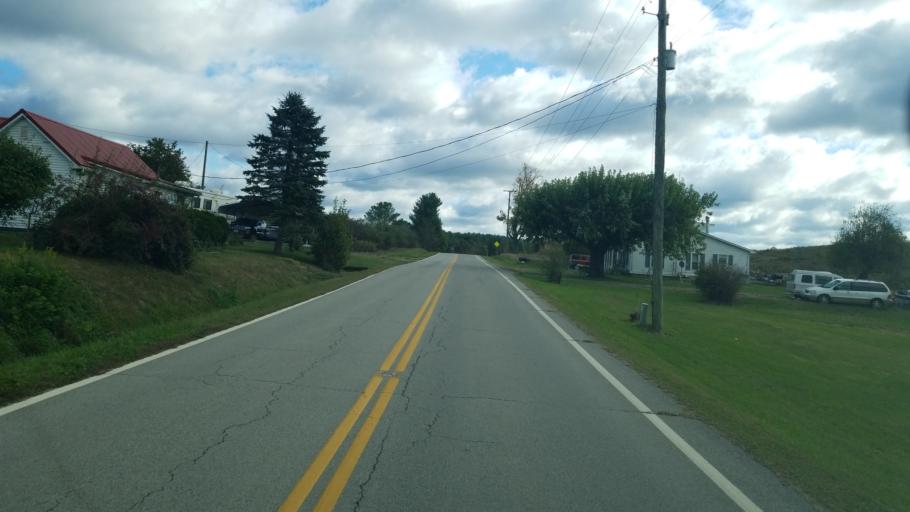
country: US
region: Ohio
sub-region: Vinton County
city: McArthur
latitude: 39.1635
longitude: -82.4570
